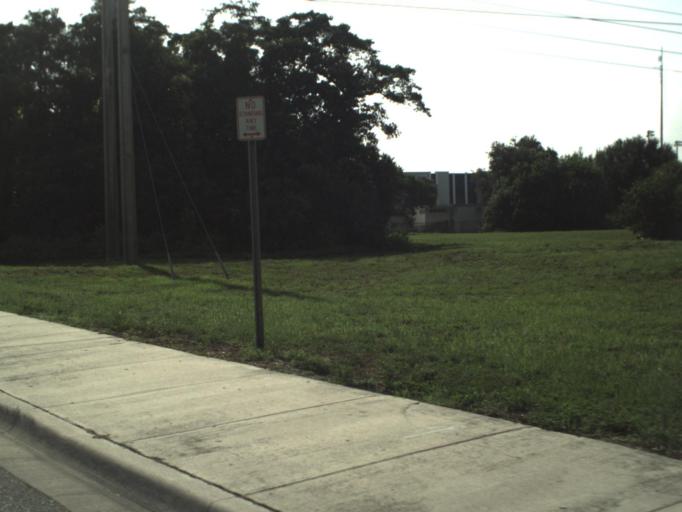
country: US
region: Florida
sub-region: Broward County
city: Margate
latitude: 26.2728
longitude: -80.2181
